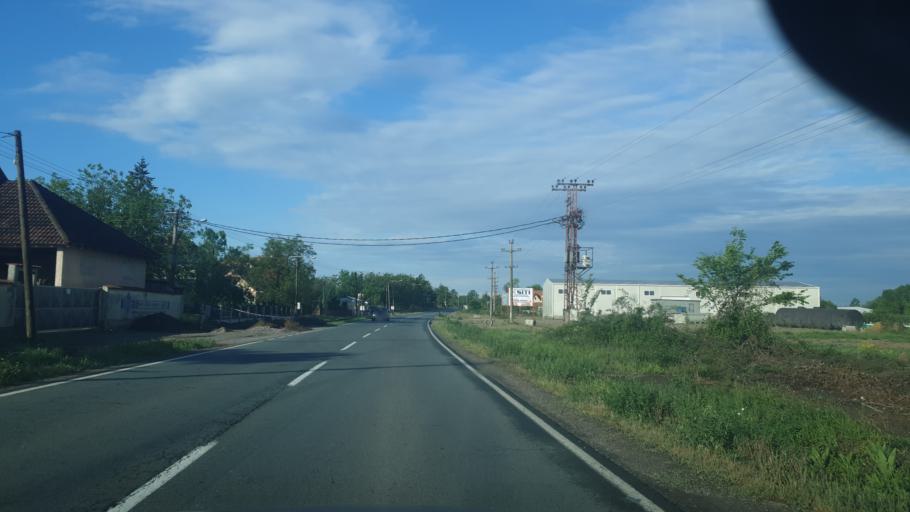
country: RS
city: Zvecka
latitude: 44.6185
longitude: 20.1692
